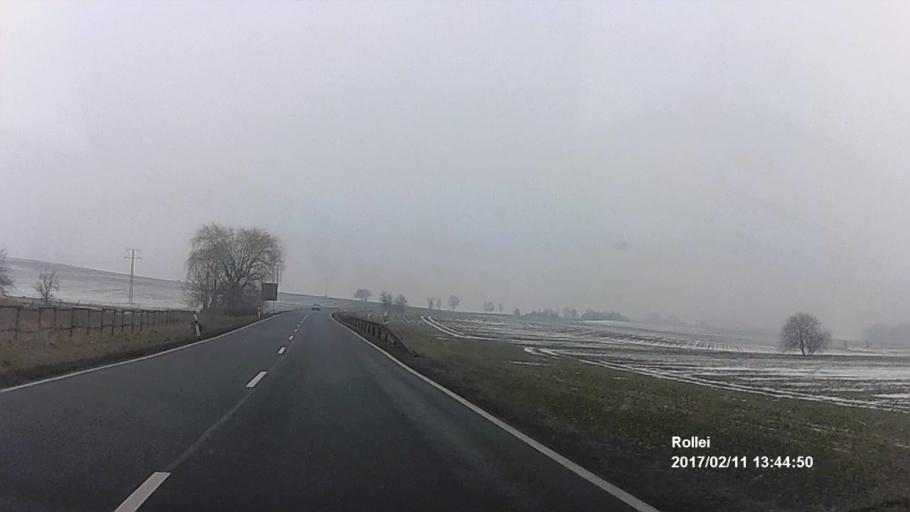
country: DE
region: Lower Saxony
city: Bad Sachsa
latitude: 51.5488
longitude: 10.5703
